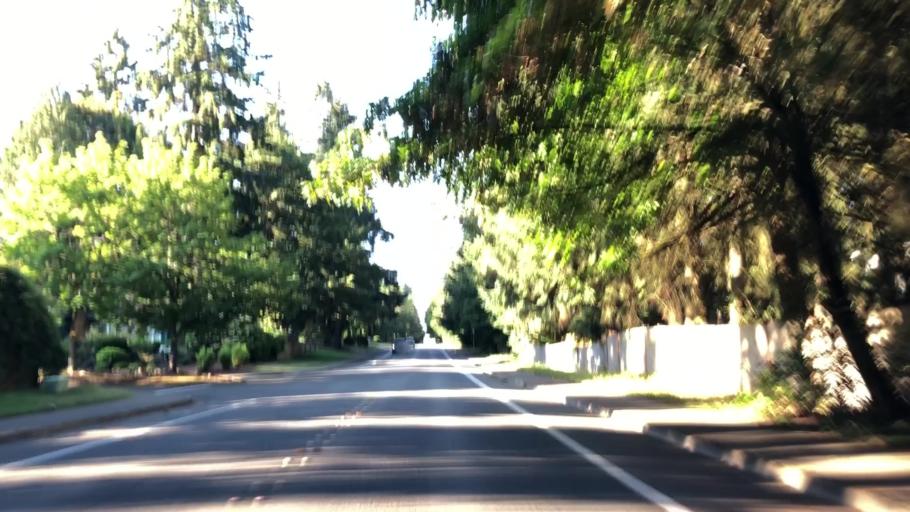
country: US
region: Washington
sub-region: King County
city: Redmond
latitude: 47.6973
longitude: -122.1191
